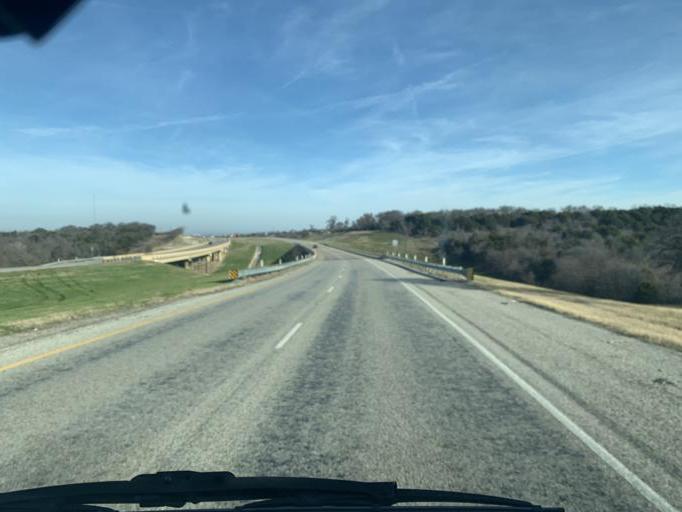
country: US
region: Texas
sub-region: Dallas County
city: Cedar Hill
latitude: 32.6350
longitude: -96.9726
